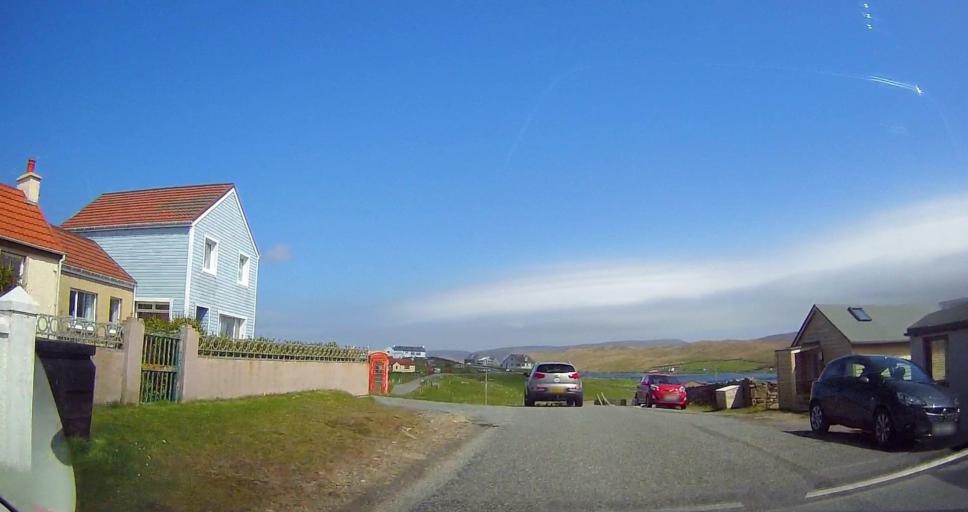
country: GB
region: Scotland
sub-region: Shetland Islands
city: Sandwick
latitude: 60.0809
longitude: -1.3358
